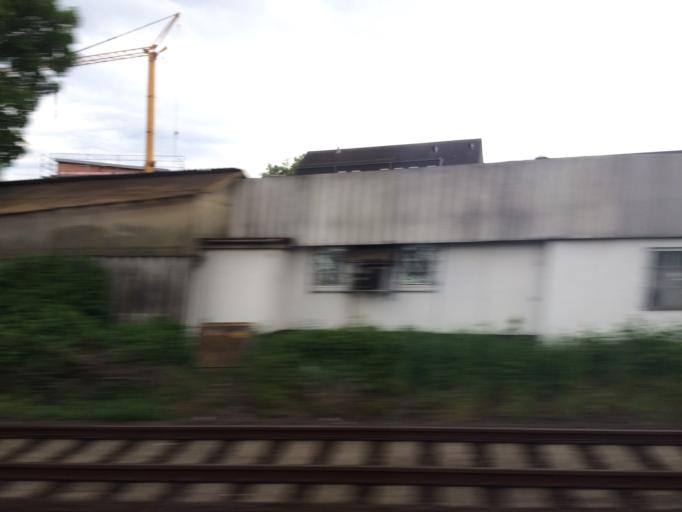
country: DE
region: Hesse
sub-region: Regierungsbezirk Darmstadt
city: Offenbach
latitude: 50.1340
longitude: 8.7661
